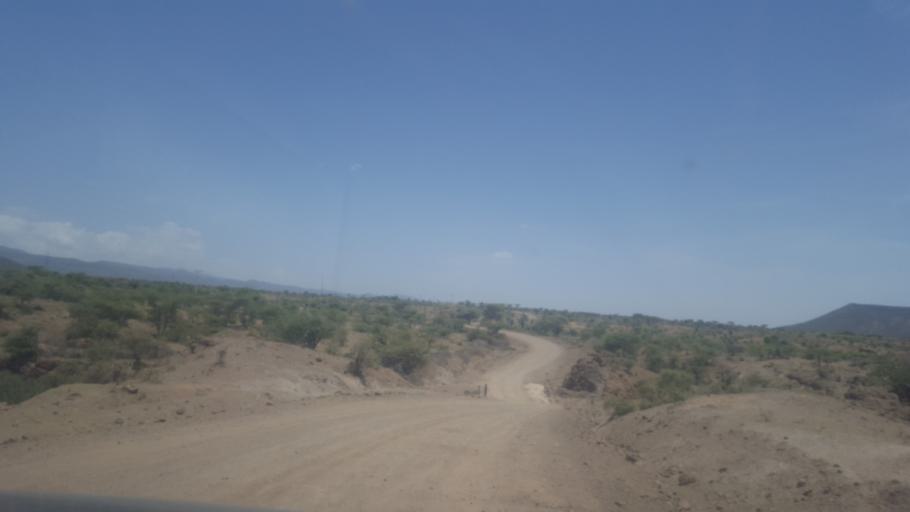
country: ET
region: Dire Dawa
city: Dire Dawa
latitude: 9.6028
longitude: 41.5826
